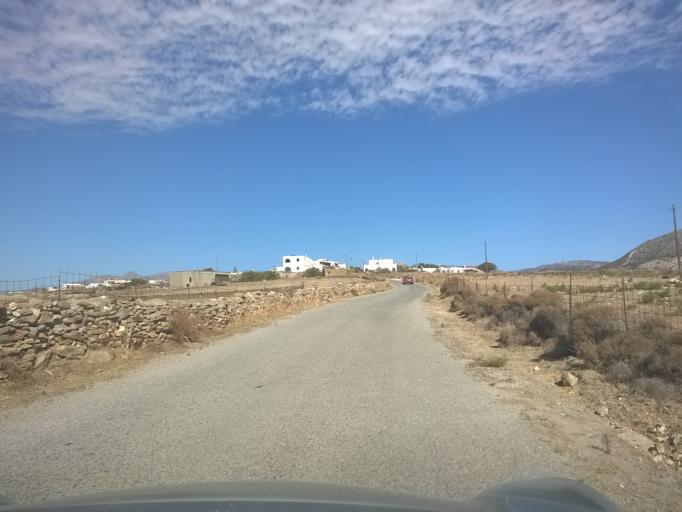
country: GR
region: South Aegean
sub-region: Nomos Kykladon
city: Filotion
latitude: 37.0381
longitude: 25.4312
